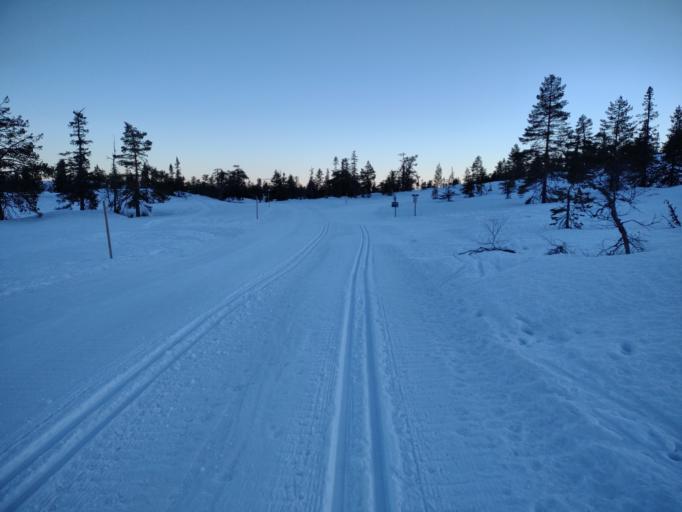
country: NO
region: Buskerud
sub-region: Flesberg
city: Lampeland
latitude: 59.7612
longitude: 9.4402
